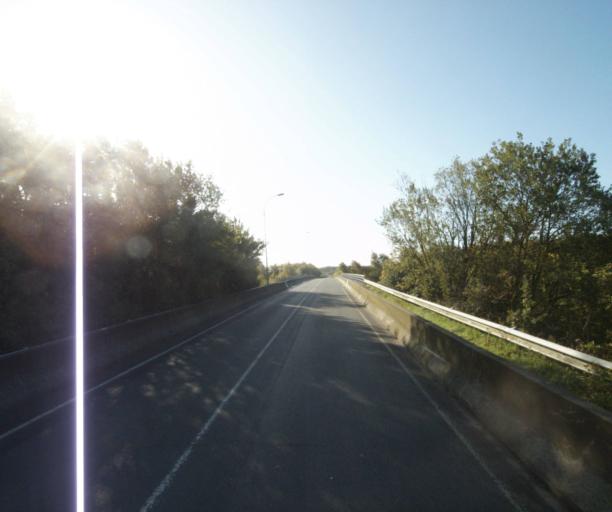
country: FR
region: Nord-Pas-de-Calais
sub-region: Departement du Nord
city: Lompret
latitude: 50.6636
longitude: 3.0106
